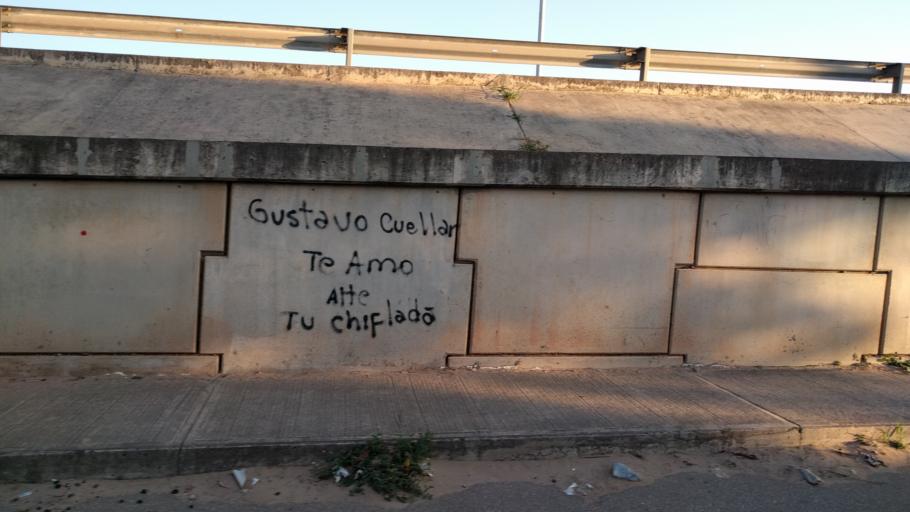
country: BO
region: Santa Cruz
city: Cotoca
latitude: -17.7648
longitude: -63.0800
